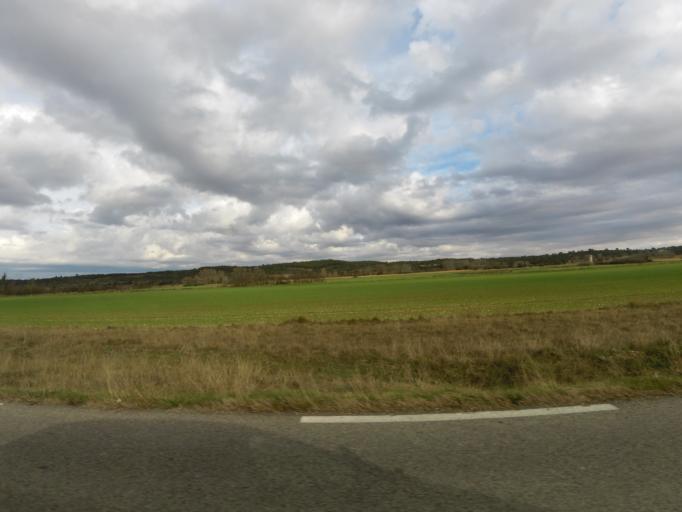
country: FR
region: Languedoc-Roussillon
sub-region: Departement du Gard
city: La Calmette
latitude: 43.8812
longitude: 4.2551
